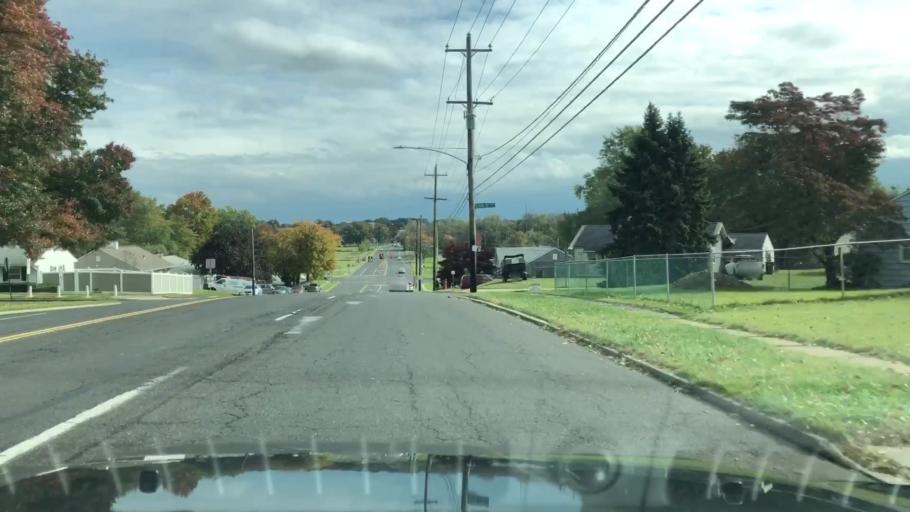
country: US
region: Pennsylvania
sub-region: Bucks County
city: Fairless Hills
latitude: 40.1766
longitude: -74.8626
